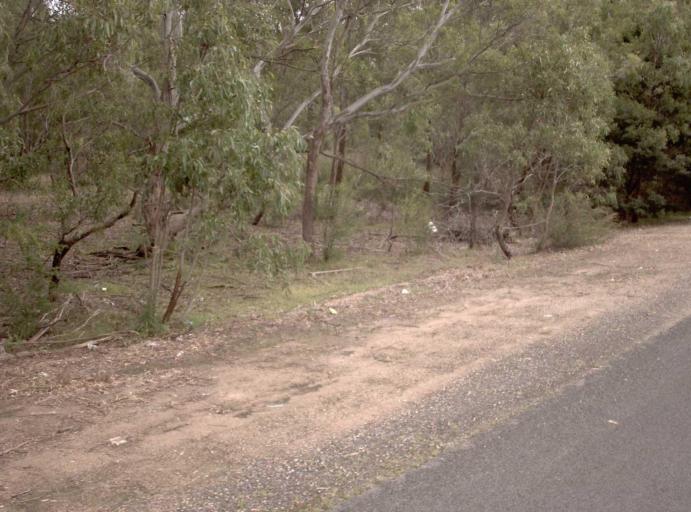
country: AU
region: Victoria
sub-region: Wellington
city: Sale
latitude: -37.9602
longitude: 147.0947
